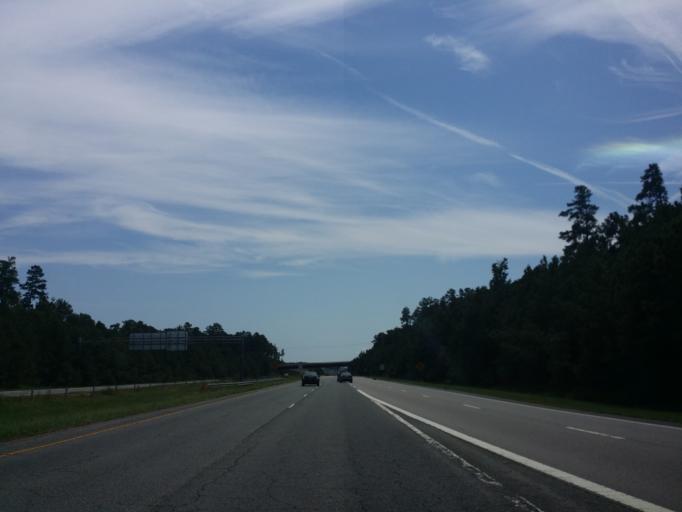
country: US
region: North Carolina
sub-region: Wake County
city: Morrisville
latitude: 35.8863
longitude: -78.8119
